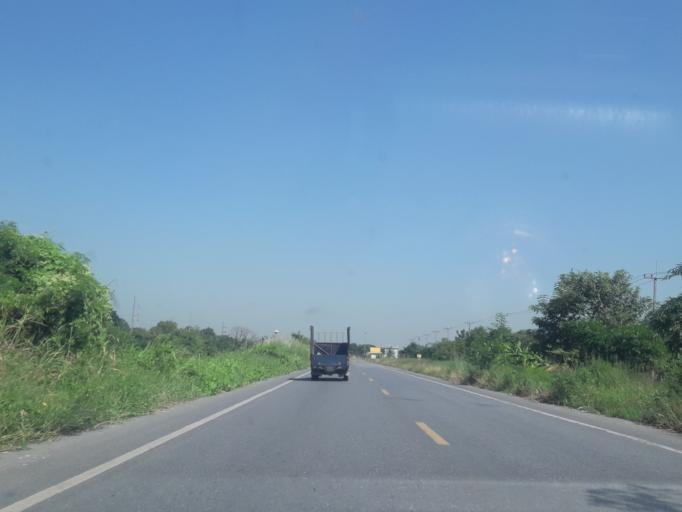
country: TH
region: Sara Buri
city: Nong Khae
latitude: 14.2624
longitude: 100.8233
